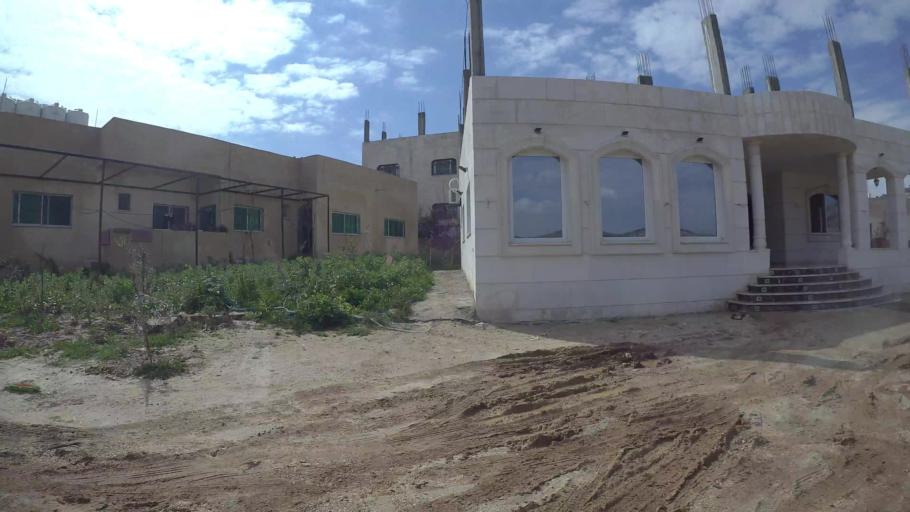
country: JO
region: Amman
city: Al Jubayhah
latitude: 32.0672
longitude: 35.8228
